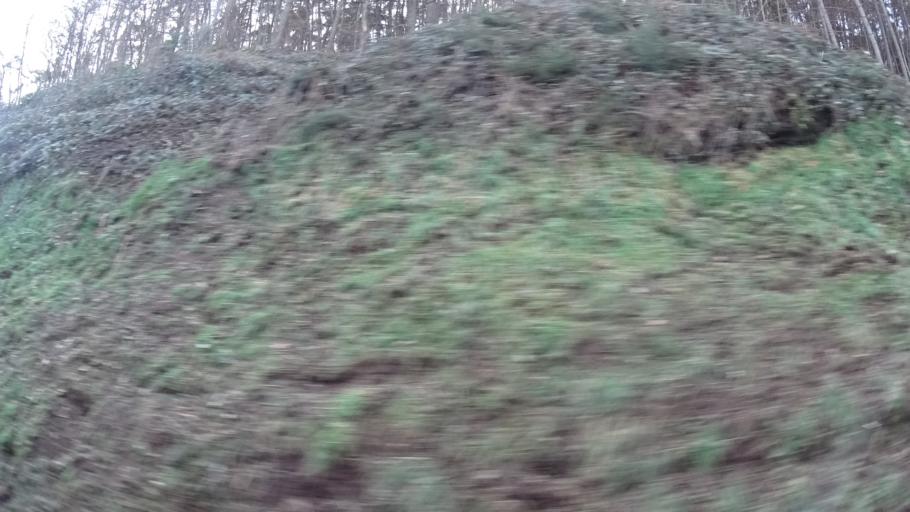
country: DE
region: Bavaria
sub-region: Regierungsbezirk Unterfranken
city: Grossheubach
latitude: 49.7389
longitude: 9.2359
